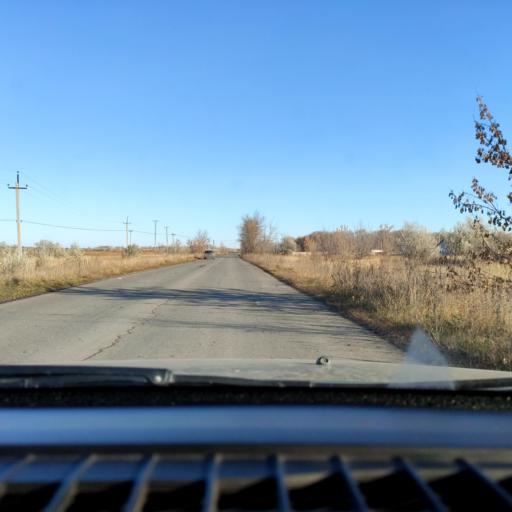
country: RU
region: Samara
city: Tol'yatti
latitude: 53.6460
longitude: 49.3187
